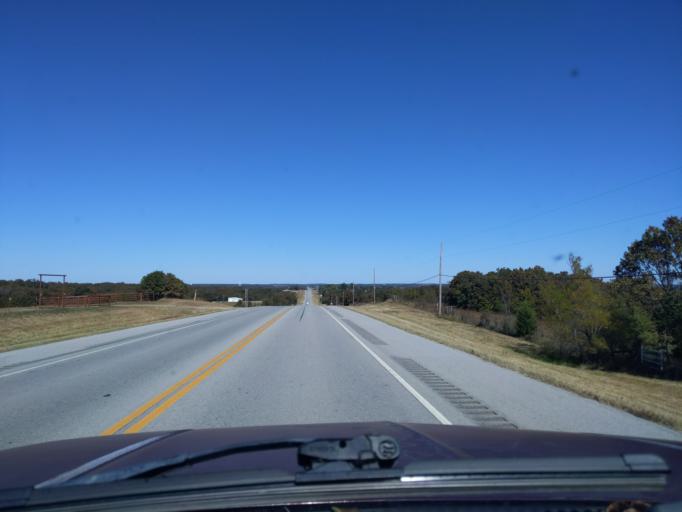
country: US
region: Oklahoma
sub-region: Creek County
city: Bristow
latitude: 35.7735
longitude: -96.3872
